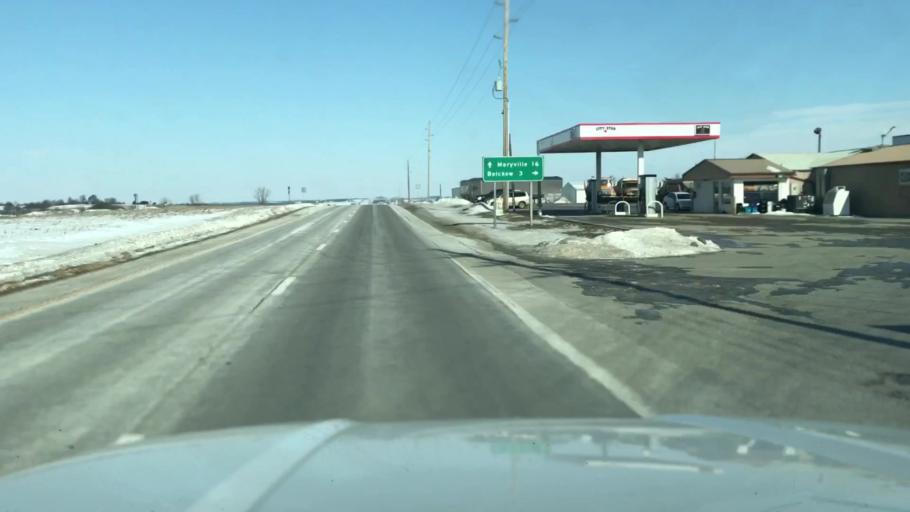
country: US
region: Missouri
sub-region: Andrew County
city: Savannah
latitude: 40.1127
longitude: -94.8697
